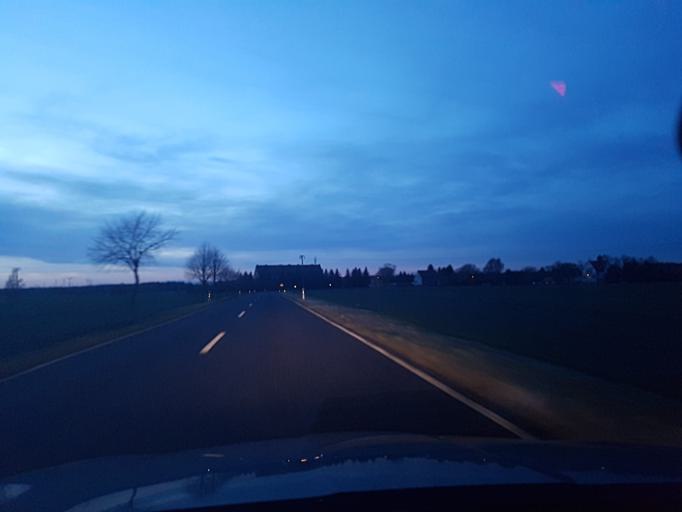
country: DE
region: Brandenburg
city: Trobitz
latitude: 51.5707
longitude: 13.4155
